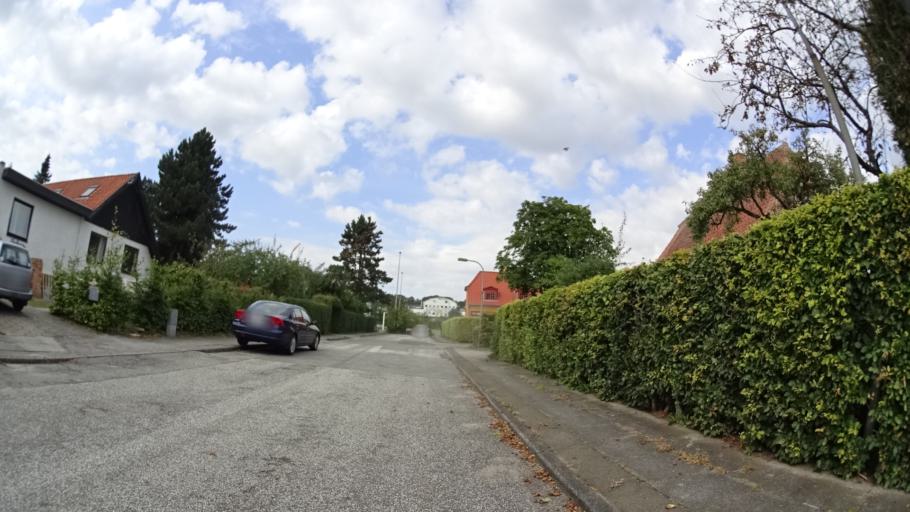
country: DK
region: Central Jutland
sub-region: Arhus Kommune
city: Stavtrup
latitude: 56.1529
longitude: 10.0972
